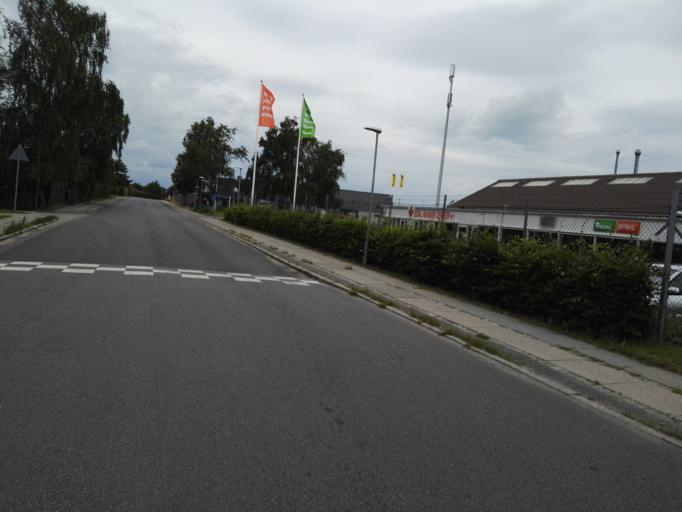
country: DK
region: Capital Region
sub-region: Egedal Kommune
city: Vekso
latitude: 55.7566
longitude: 12.2359
